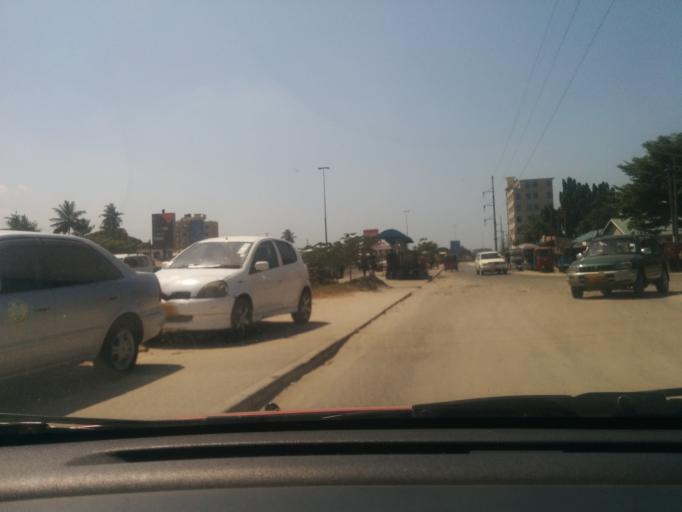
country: TZ
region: Dar es Salaam
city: Magomeni
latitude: -6.7711
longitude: 39.2235
